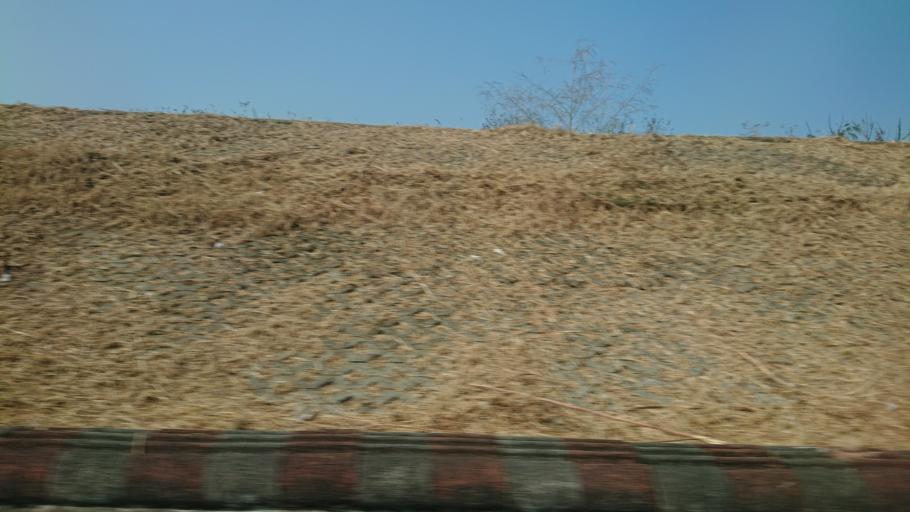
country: TW
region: Taiwan
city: Lugu
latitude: 23.7493
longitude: 120.6588
